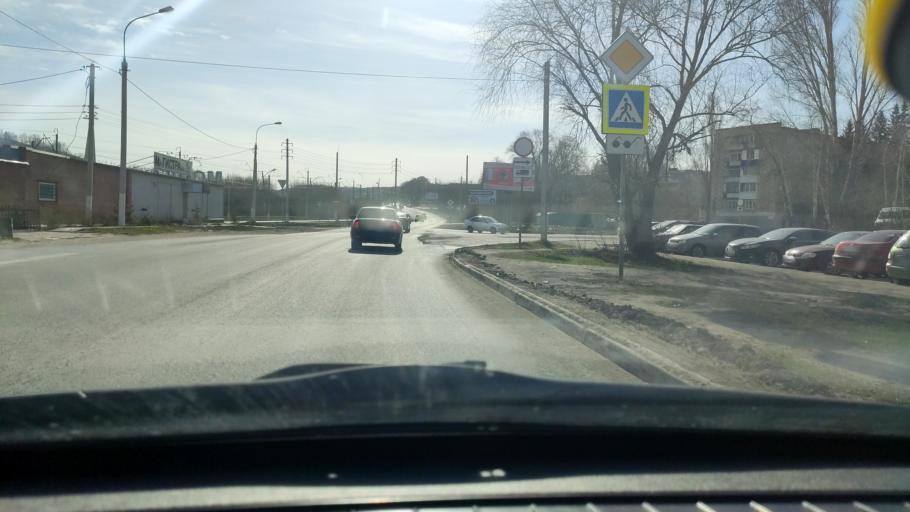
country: RU
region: Samara
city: Zhigulevsk
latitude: 53.4078
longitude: 49.4861
